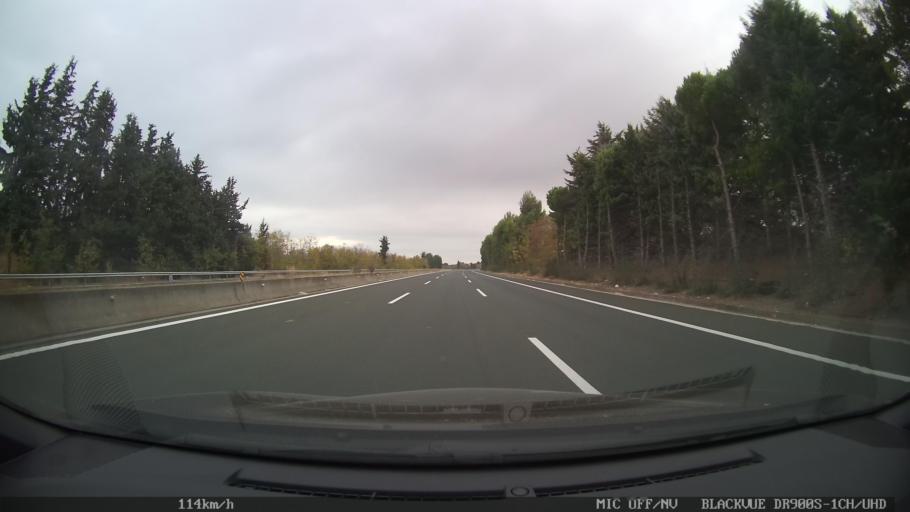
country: GR
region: Central Macedonia
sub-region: Nomos Pierias
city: Makrygialos
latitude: 40.3947
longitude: 22.6027
